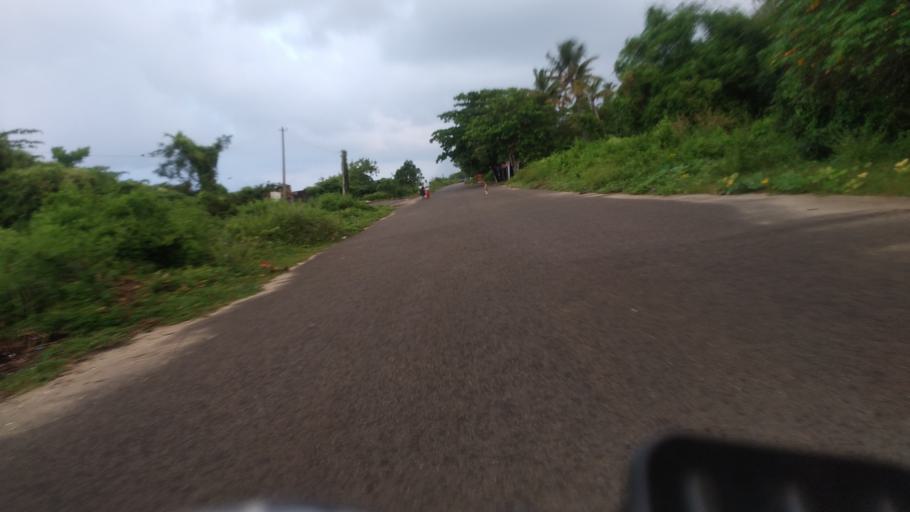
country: IN
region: Kerala
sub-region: Ernakulam
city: Cochin
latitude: 9.9999
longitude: 76.2205
